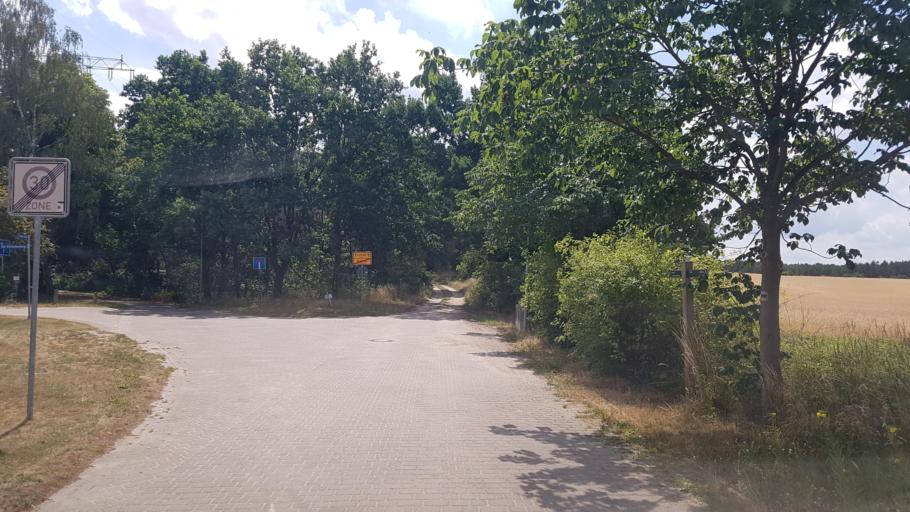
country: DE
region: Brandenburg
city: Brandenburg an der Havel
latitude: 52.3626
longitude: 12.5556
